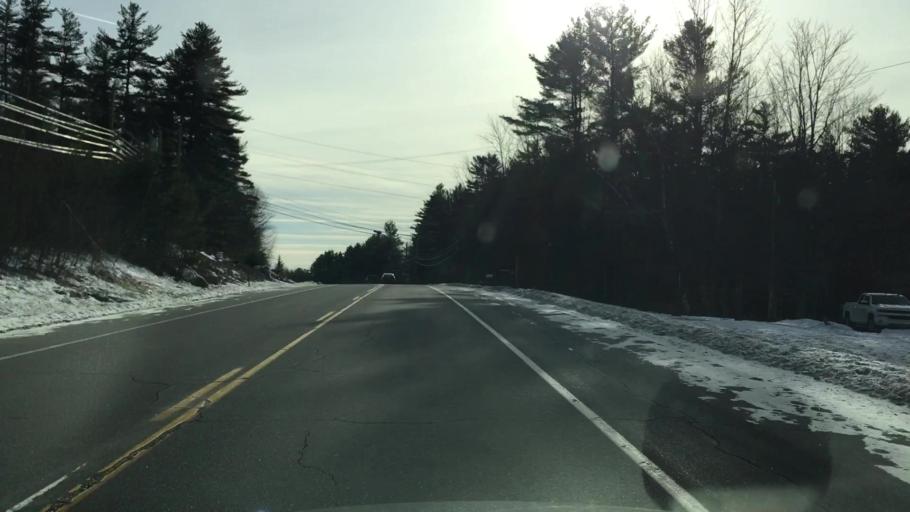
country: US
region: New Hampshire
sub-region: Sullivan County
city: Sunapee
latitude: 43.4121
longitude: -72.0838
